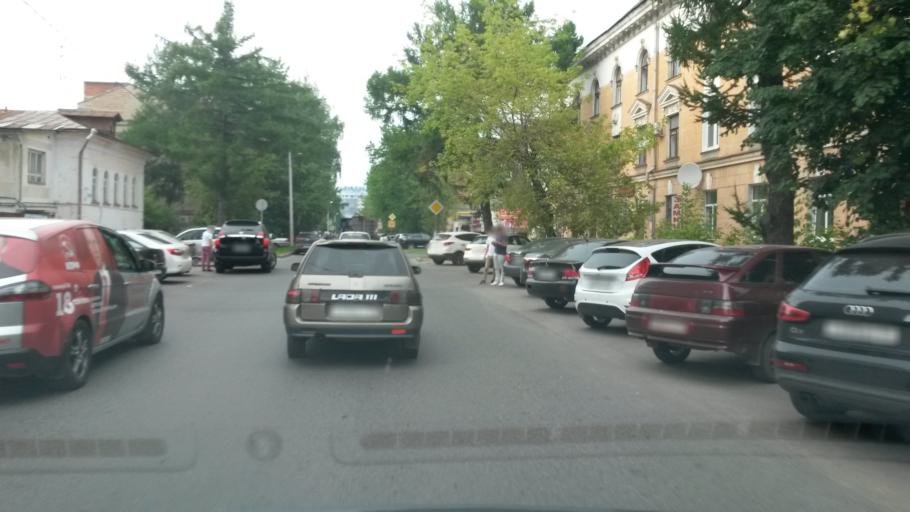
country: RU
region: Ivanovo
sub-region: Gorod Ivanovo
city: Ivanovo
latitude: 56.9945
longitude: 40.9741
